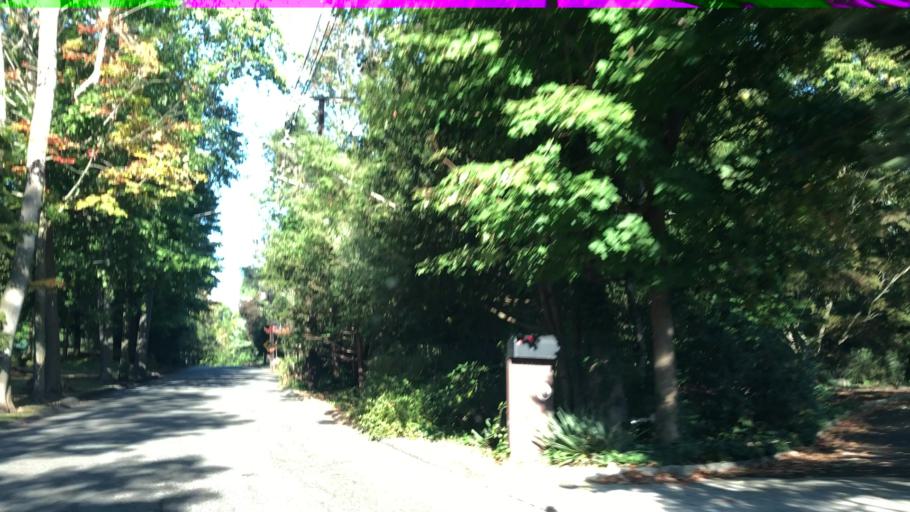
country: US
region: New Jersey
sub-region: Bergen County
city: Woodcliff Lake
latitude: 41.0324
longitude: -74.0610
